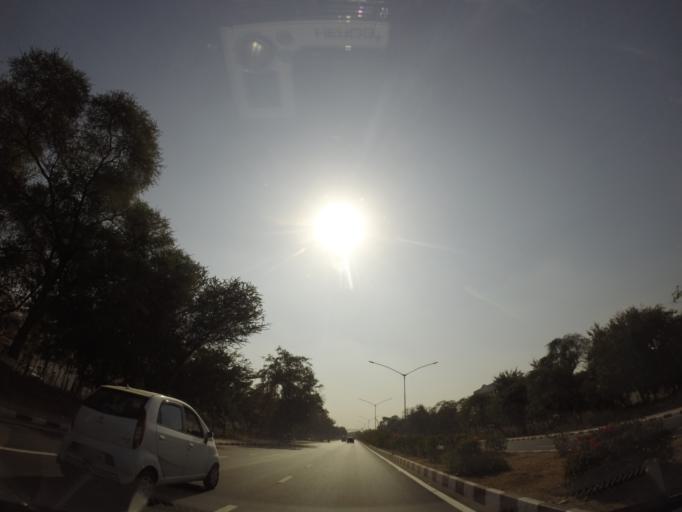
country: IN
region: Gujarat
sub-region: Gandhinagar
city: Ghandinagar
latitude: 23.2065
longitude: 72.6349
